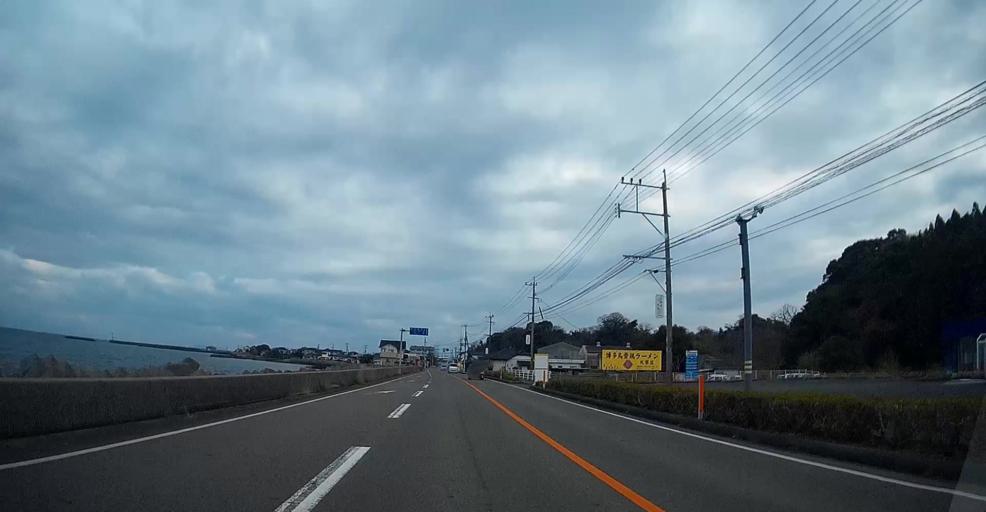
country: JP
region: Kumamoto
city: Hondo
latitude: 32.4695
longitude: 130.2499
